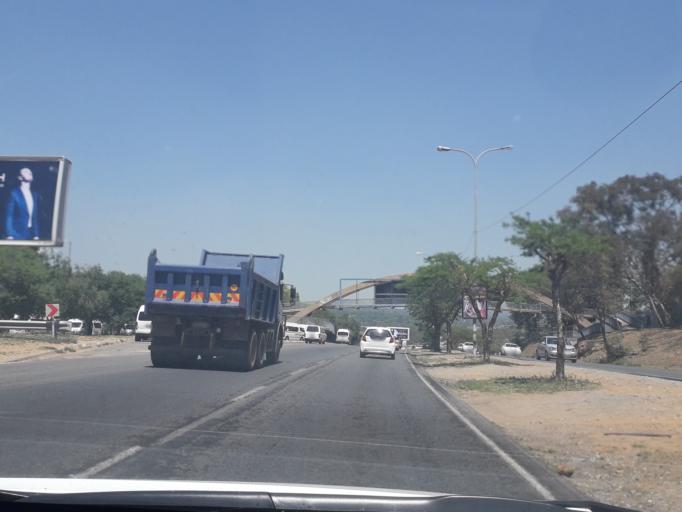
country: ZA
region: Gauteng
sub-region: City of Johannesburg Metropolitan Municipality
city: Johannesburg
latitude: -26.0730
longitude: 28.0267
